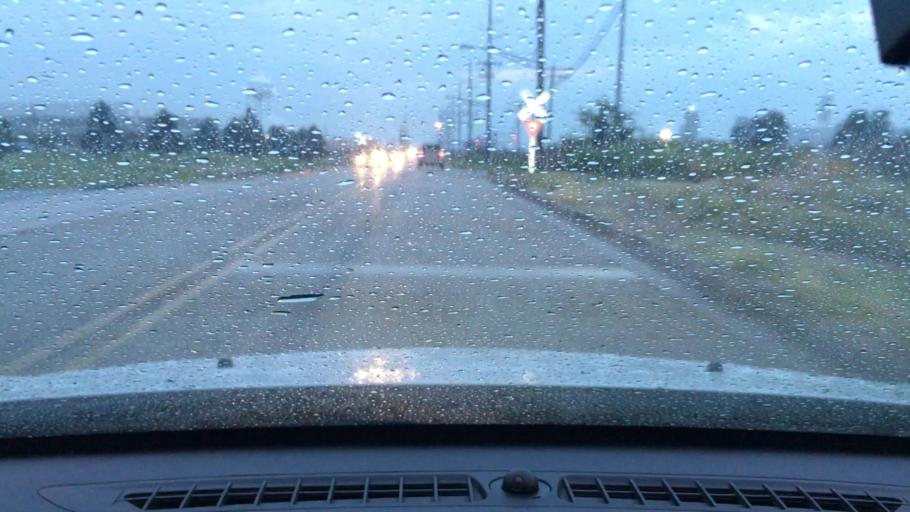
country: US
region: Illinois
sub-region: Ogle County
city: Rochelle
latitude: 41.9133
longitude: -89.0494
